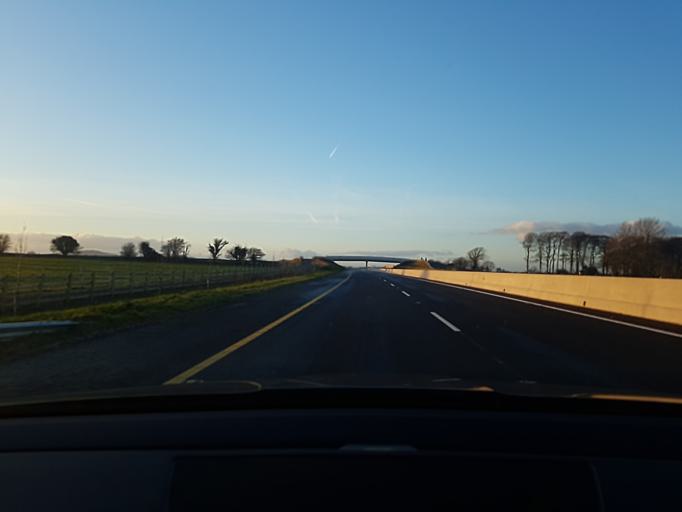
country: IE
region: Connaught
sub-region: County Galway
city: Tuam
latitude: 53.4629
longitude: -8.8532
